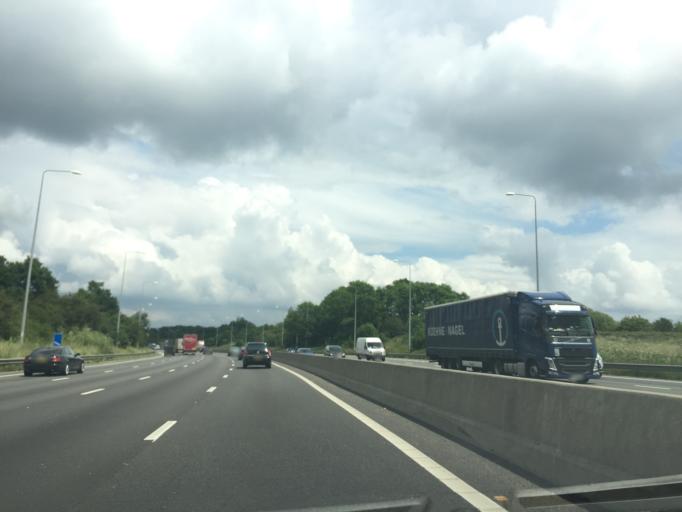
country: GB
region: England
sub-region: Hertfordshire
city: Potters Bar
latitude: 51.6840
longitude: -0.1794
